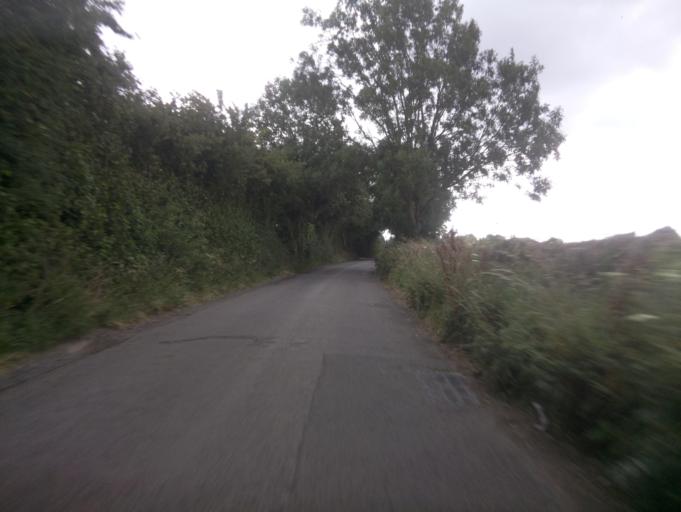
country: GB
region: England
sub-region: Gloucestershire
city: Shurdington
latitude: 51.7979
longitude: -2.1240
